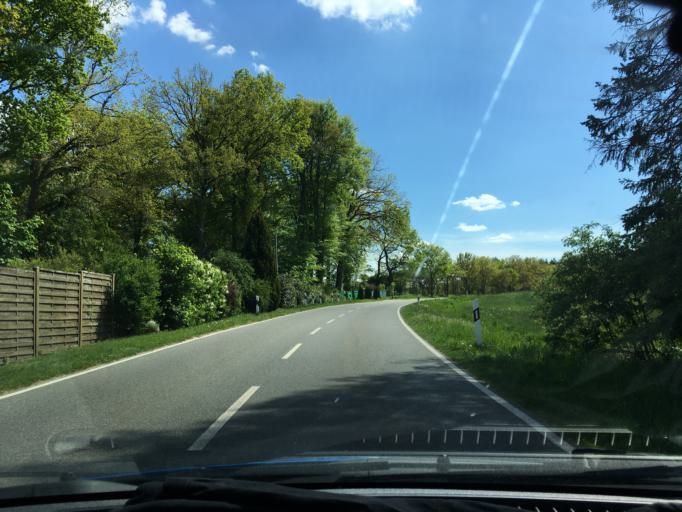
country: DE
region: Lower Saxony
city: Zernien
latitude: 53.0646
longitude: 10.8888
